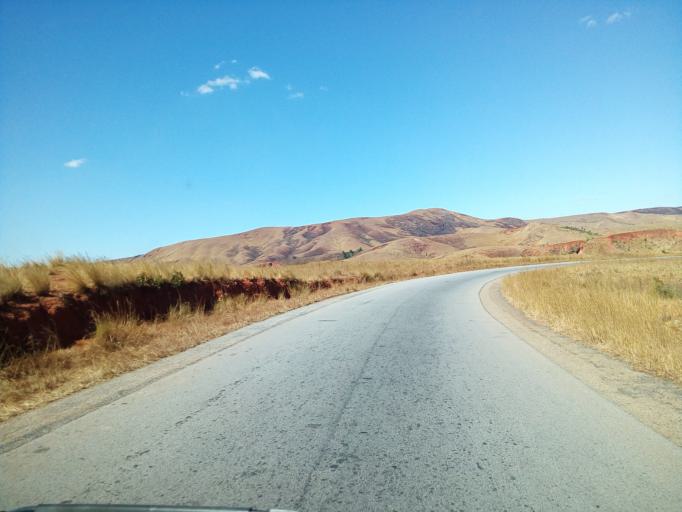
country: MG
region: Betsiboka
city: Maevatanana
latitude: -17.4176
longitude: 46.9277
